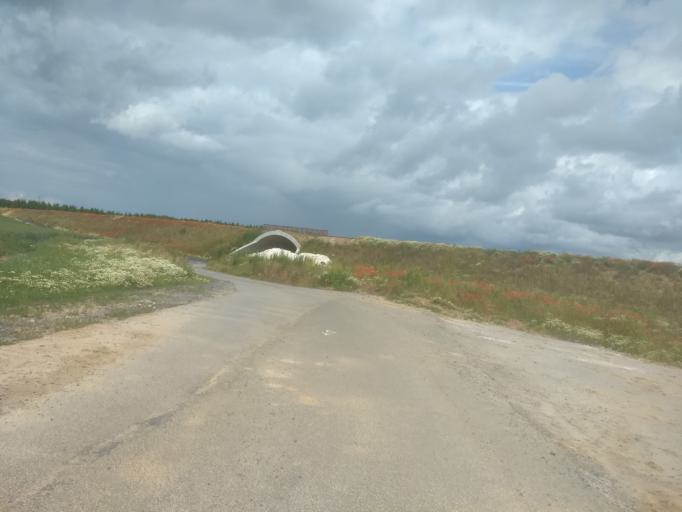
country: FR
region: Nord-Pas-de-Calais
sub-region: Departement du Pas-de-Calais
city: Dainville
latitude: 50.2647
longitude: 2.7126
